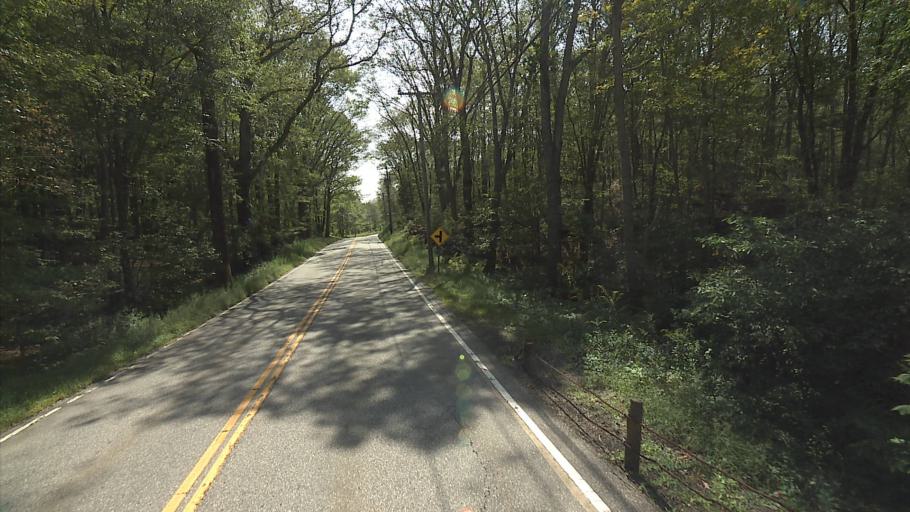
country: US
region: Connecticut
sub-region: Windham County
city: East Brooklyn
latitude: 41.8085
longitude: -71.9536
